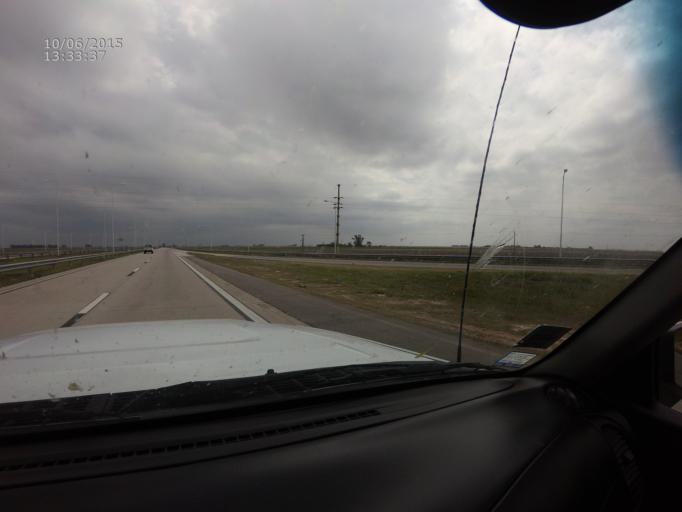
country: AR
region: Cordoba
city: Leones
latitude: -32.6225
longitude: -62.3319
